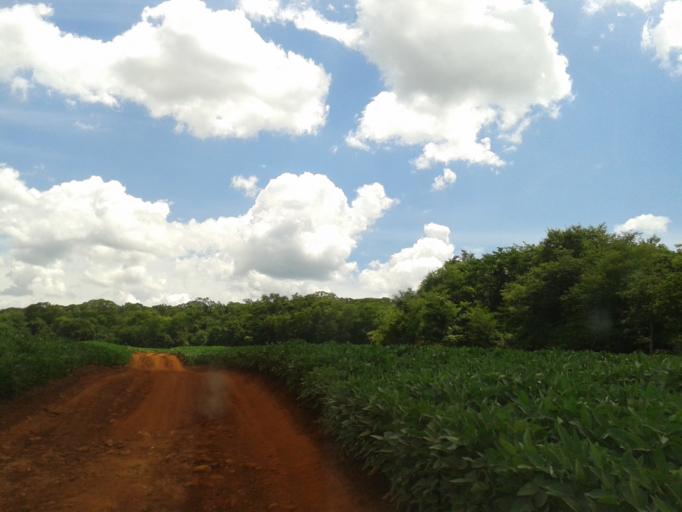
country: BR
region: Minas Gerais
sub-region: Centralina
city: Centralina
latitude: -18.6828
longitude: -49.2187
